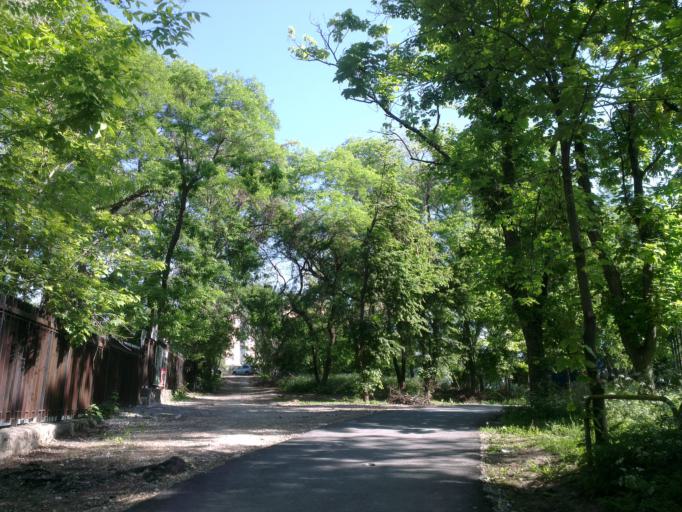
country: MD
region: Chisinau
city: Chisinau
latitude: 47.0179
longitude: 28.8066
